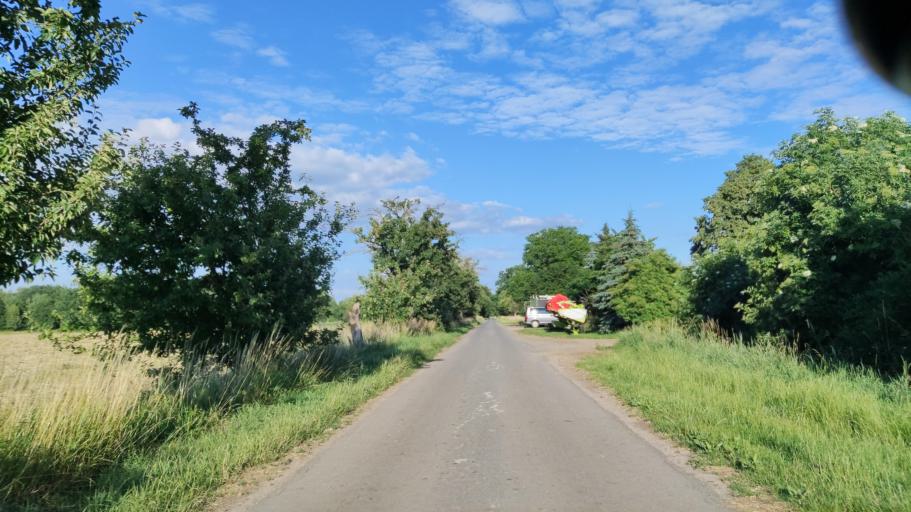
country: DE
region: Brandenburg
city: Lanz
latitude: 53.0408
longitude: 11.5430
